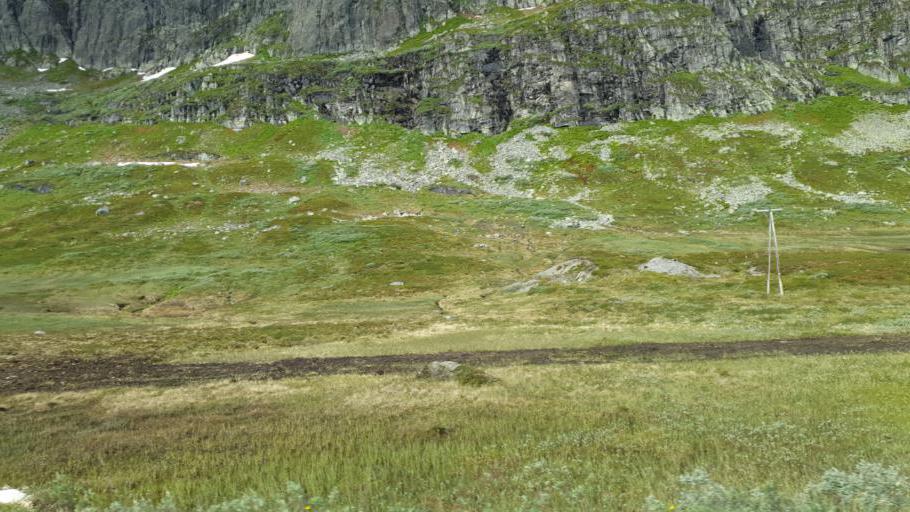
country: NO
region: Oppland
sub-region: Vestre Slidre
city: Slidre
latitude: 61.3024
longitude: 8.8078
